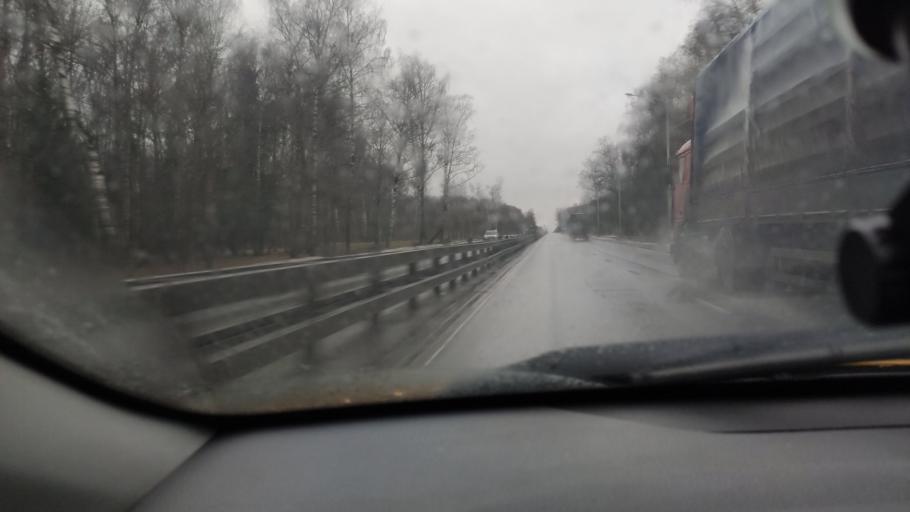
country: RU
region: Moskovskaya
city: Troitsk
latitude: 55.3620
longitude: 37.3647
